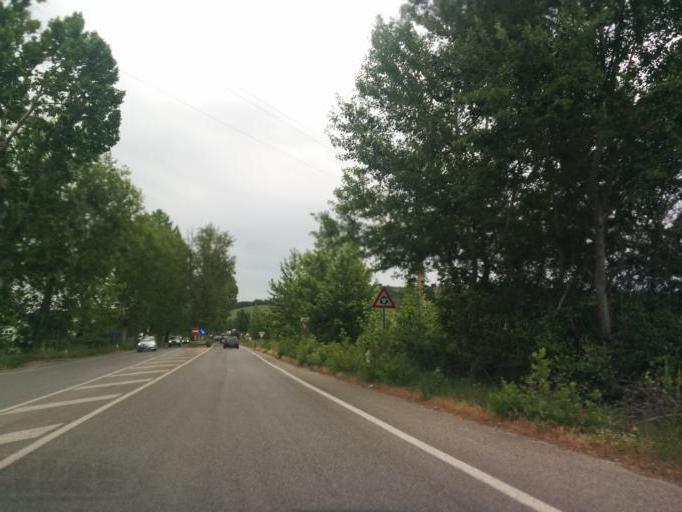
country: IT
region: Tuscany
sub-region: Provincia di Siena
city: Poggibonsi
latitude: 43.4592
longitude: 11.1074
